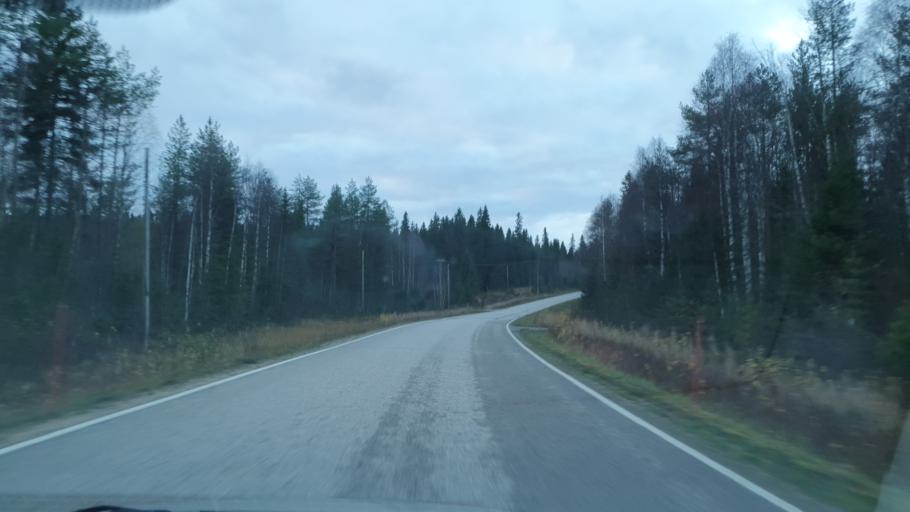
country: FI
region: Kainuu
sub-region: Kajaani
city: Ristijaervi
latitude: 64.4279
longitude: 28.3813
